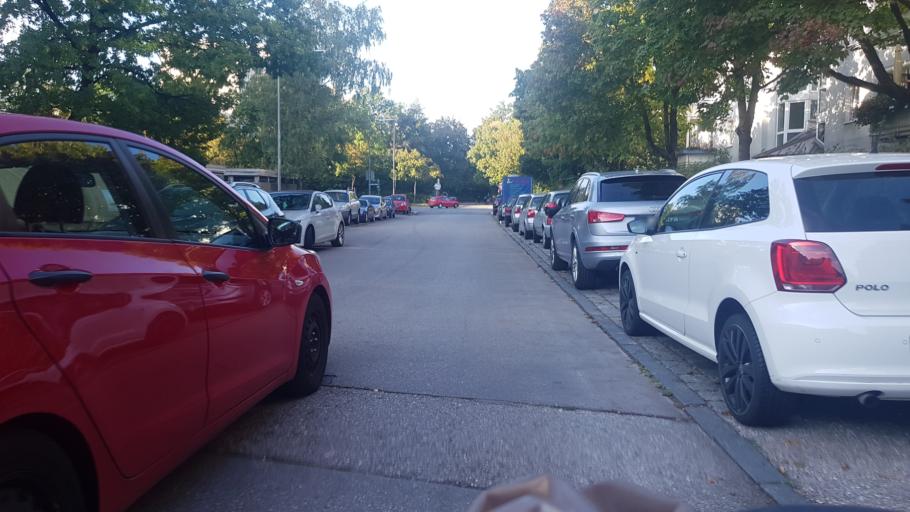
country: DE
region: Bavaria
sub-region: Upper Bavaria
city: Neubiberg
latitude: 48.1082
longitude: 11.6529
